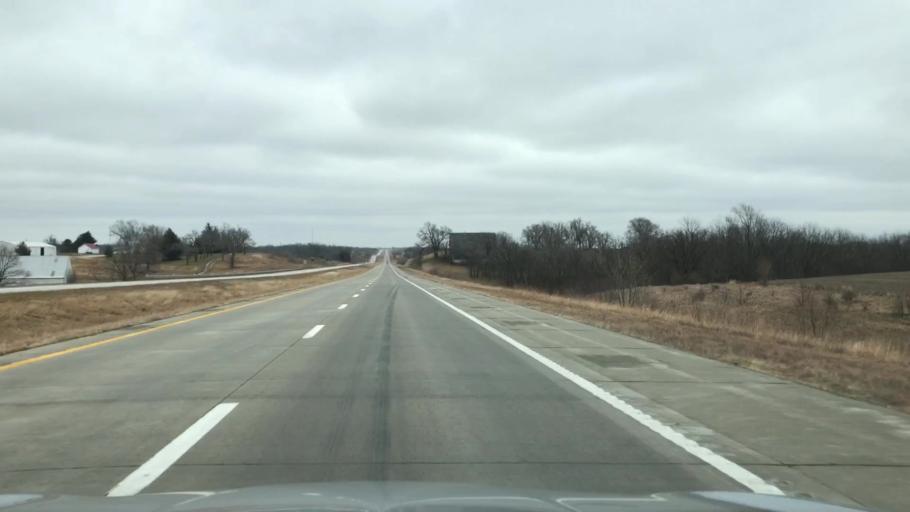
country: US
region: Missouri
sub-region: Caldwell County
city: Hamilton
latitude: 39.7350
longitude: -93.8397
